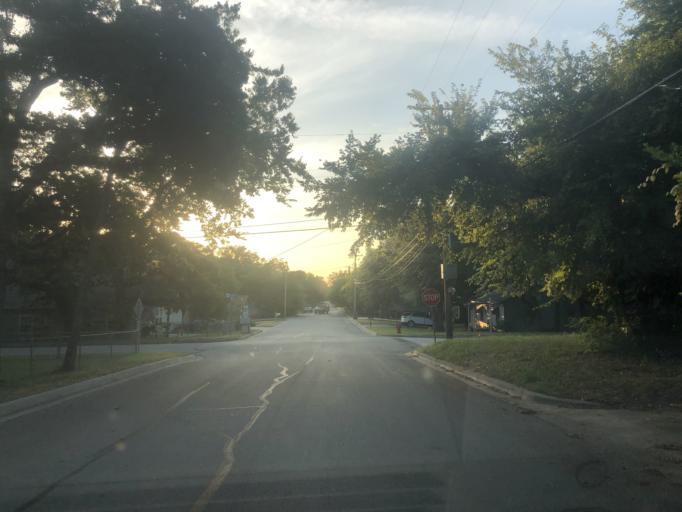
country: US
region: Texas
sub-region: Tarrant County
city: Lake Worth
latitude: 32.8021
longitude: -97.4487
